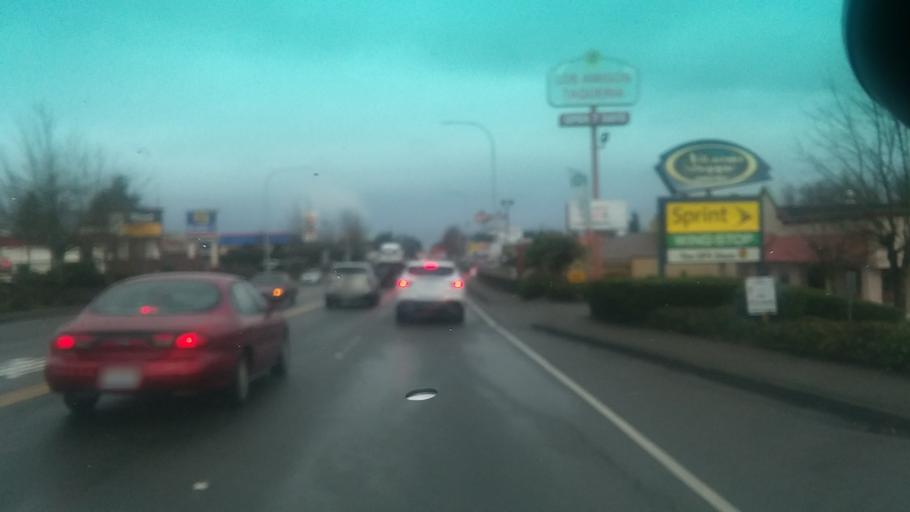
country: US
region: Washington
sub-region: Pierce County
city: South Hill
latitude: 47.1516
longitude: -122.2929
